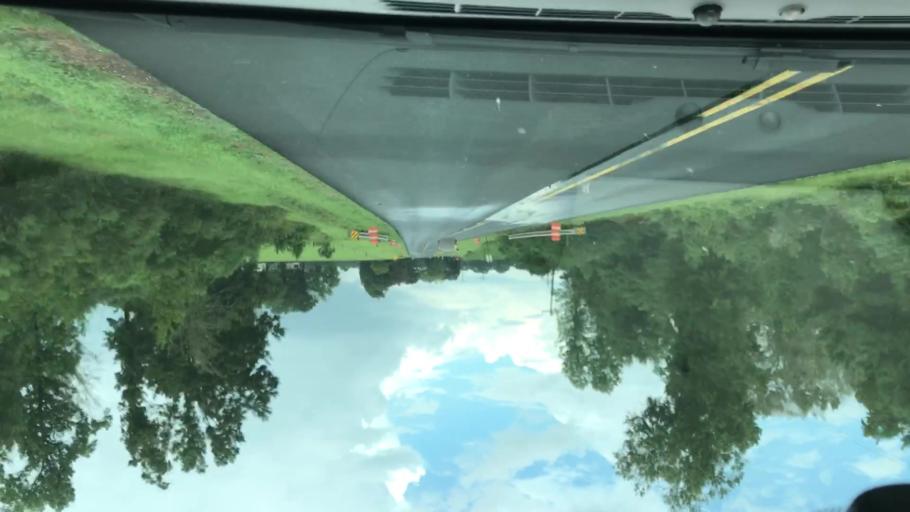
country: US
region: Georgia
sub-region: Early County
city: Blakely
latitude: 31.4251
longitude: -84.9663
